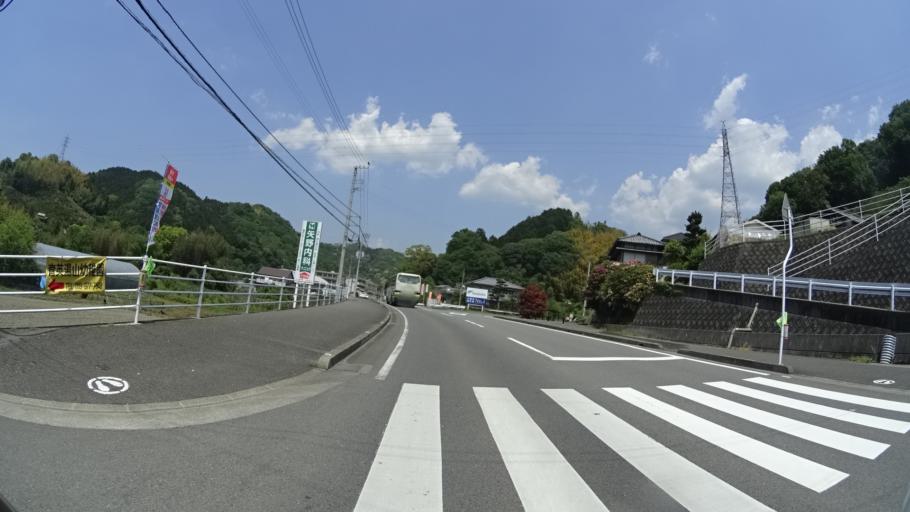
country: JP
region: Ehime
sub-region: Shikoku-chuo Shi
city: Matsuyama
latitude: 33.8579
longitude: 132.8127
